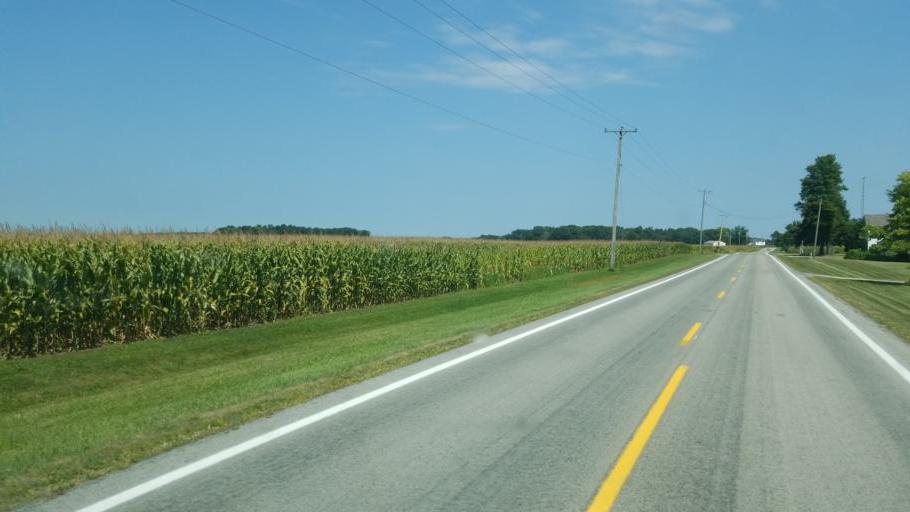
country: US
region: Ohio
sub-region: Marion County
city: Marion
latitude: 40.7049
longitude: -83.1401
